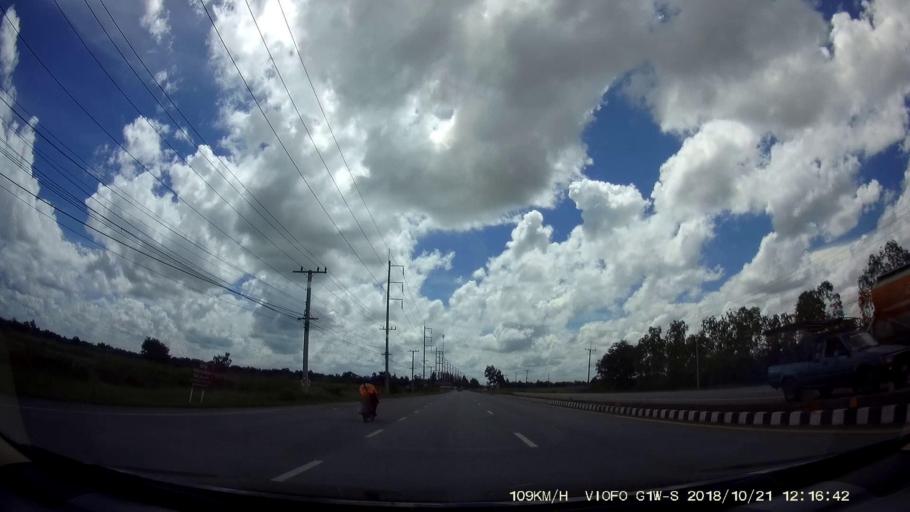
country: TH
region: Nakhon Ratchasima
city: Dan Khun Thot
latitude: 15.3432
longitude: 101.8245
